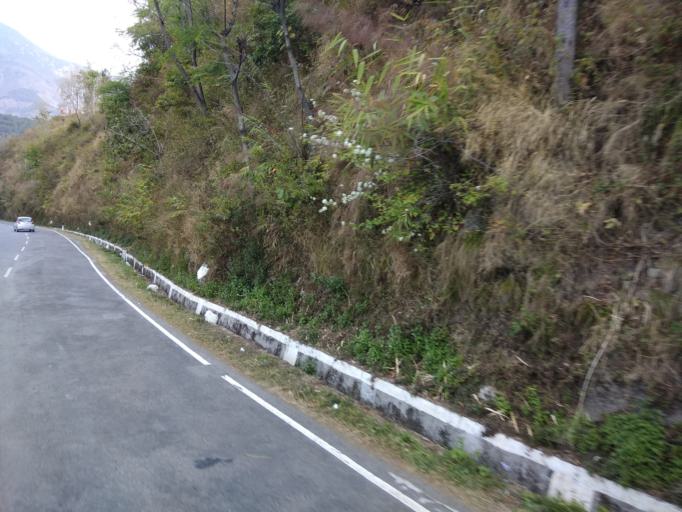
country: IN
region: Himachal Pradesh
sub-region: Kangra
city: Dharmsala
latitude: 32.1582
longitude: 76.4059
